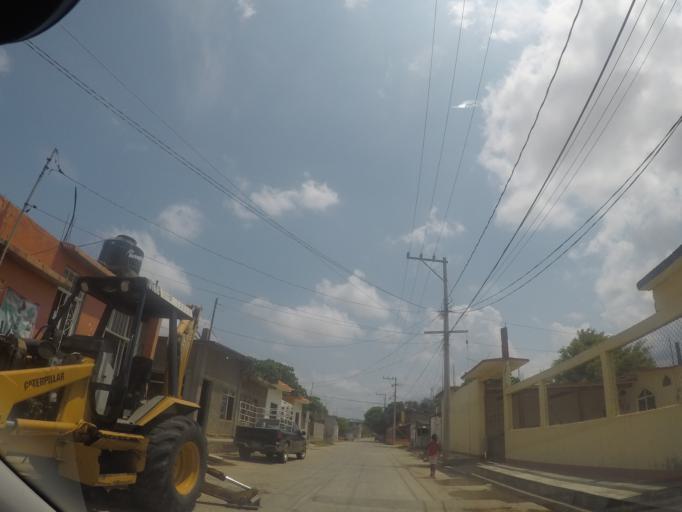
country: MX
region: Oaxaca
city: El Espinal
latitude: 16.5558
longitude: -94.9476
